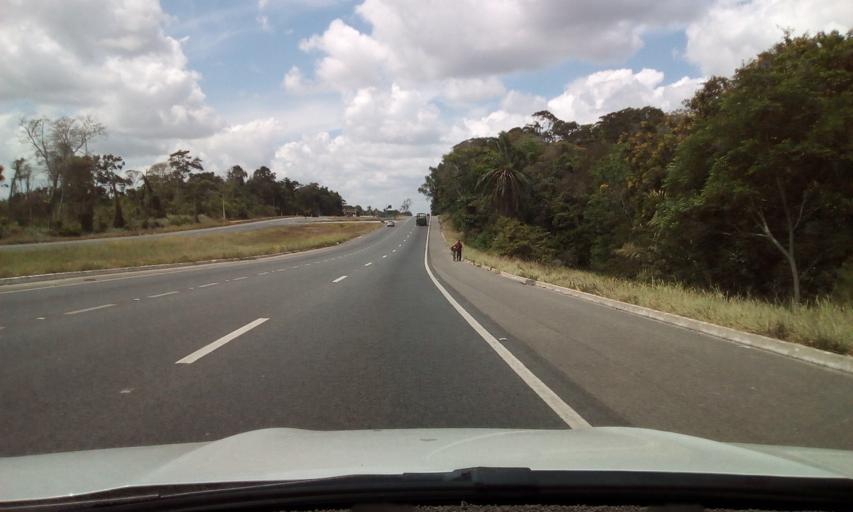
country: BR
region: Paraiba
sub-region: Santa Rita
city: Santa Rita
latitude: -7.1436
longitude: -34.9971
